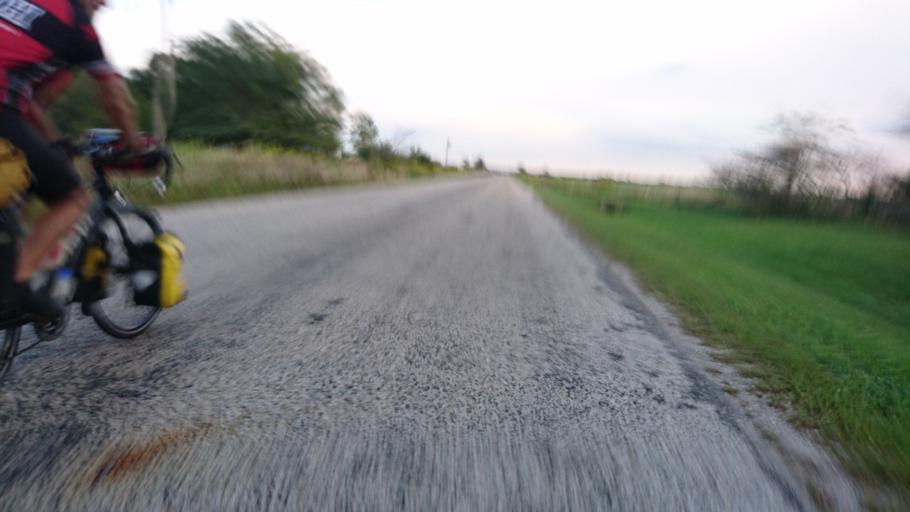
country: US
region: Illinois
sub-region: Logan County
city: Atlanta
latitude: 40.2281
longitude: -89.2030
